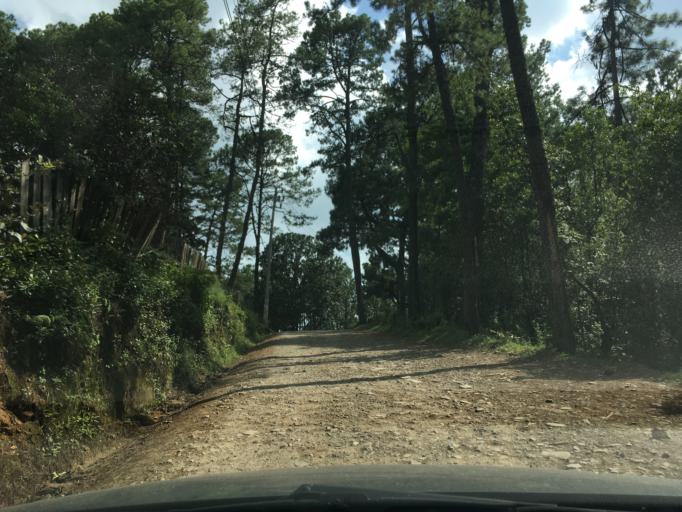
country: MX
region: Michoacan
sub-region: Morelia
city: Morelos
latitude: 19.5342
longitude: -101.1988
